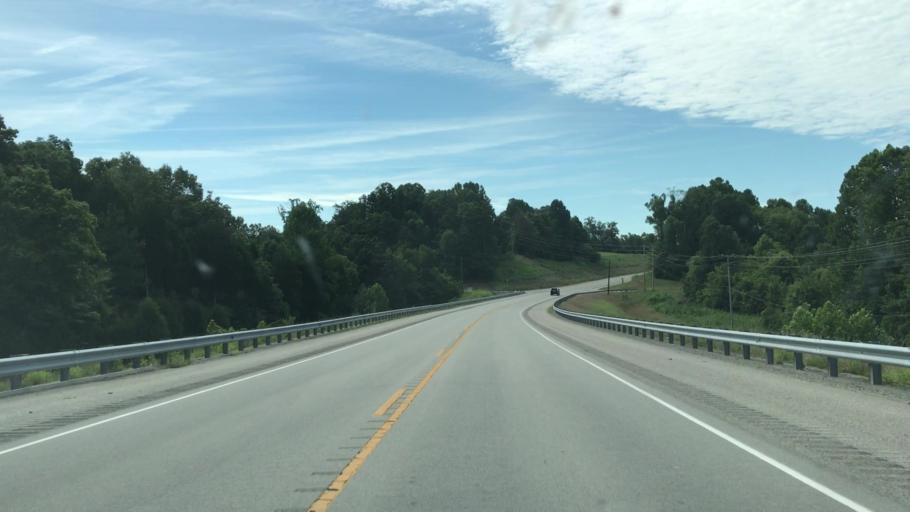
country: US
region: Kentucky
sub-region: Edmonson County
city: Brownsville
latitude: 37.1625
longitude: -86.2241
